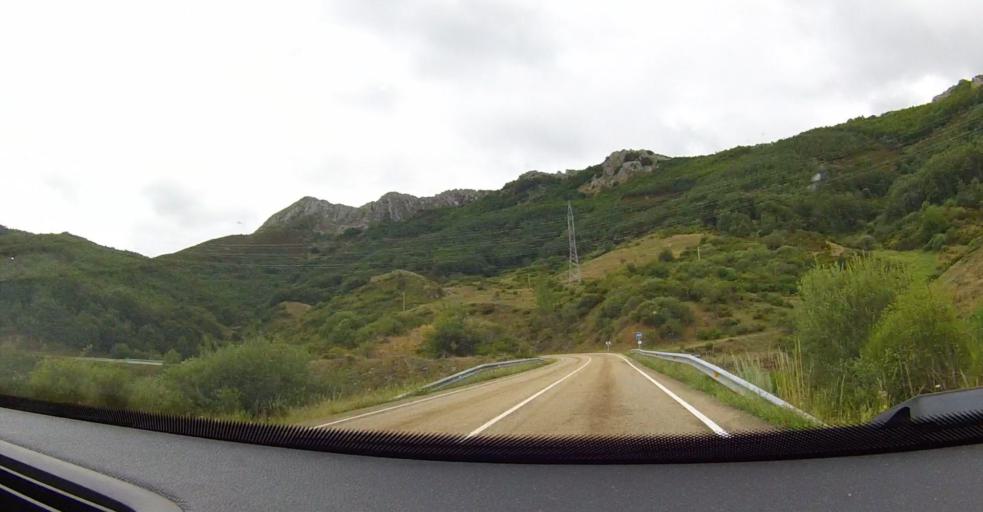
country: ES
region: Castille and Leon
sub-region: Provincia de Leon
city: Puebla de Lillo
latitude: 42.9340
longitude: -5.2745
